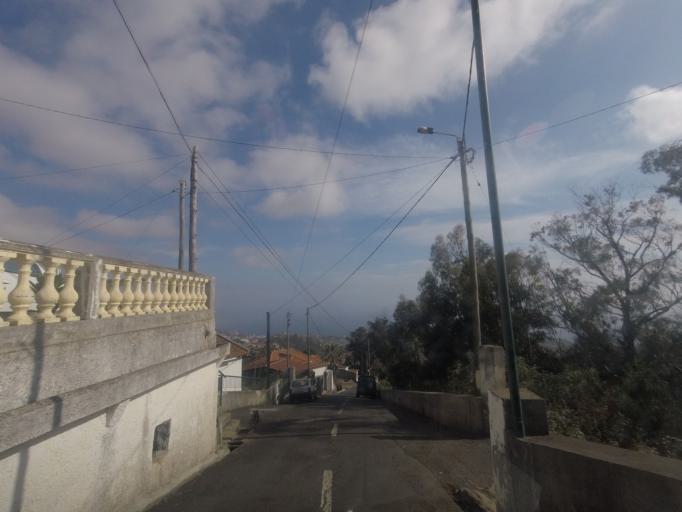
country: PT
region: Madeira
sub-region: Camara de Lobos
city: Curral das Freiras
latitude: 32.6782
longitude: -16.9538
